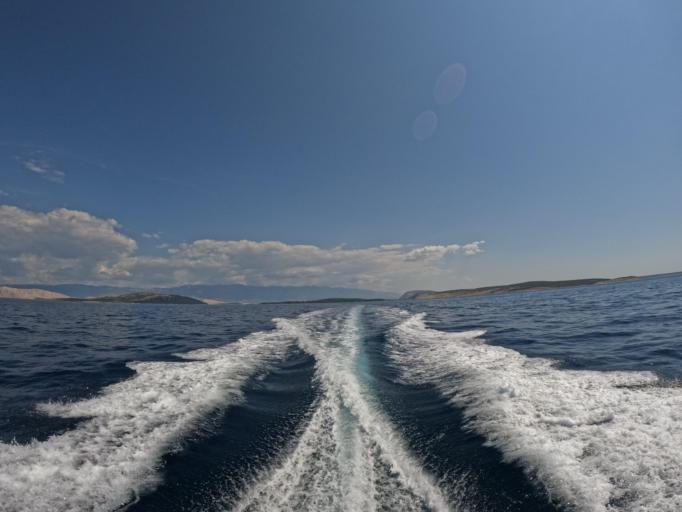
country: HR
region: Primorsko-Goranska
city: Lopar
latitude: 44.8680
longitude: 14.6794
